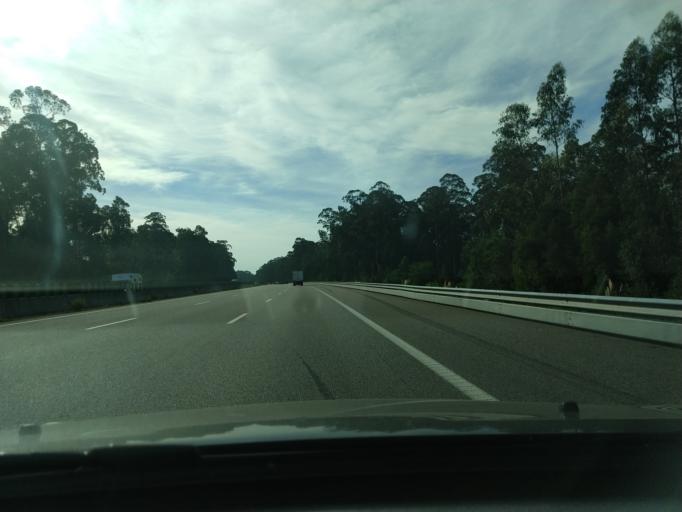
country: PT
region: Aveiro
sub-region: Ovar
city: Valega
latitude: 40.8672
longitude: -8.5596
